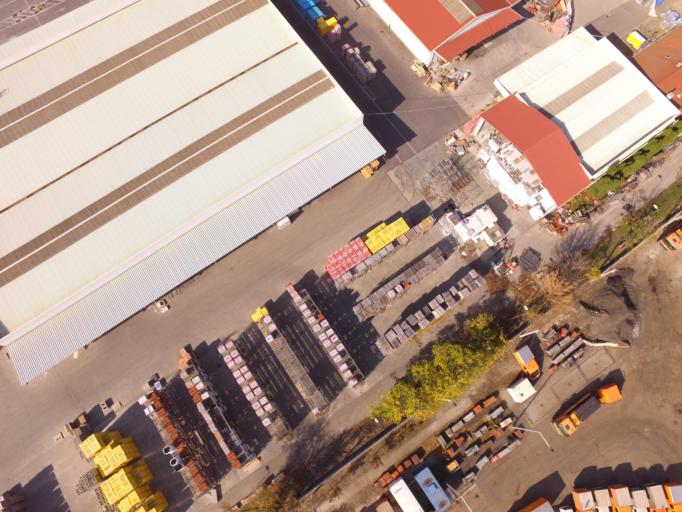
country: HU
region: Budapest
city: Budapest XX. keruelet
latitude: 47.4733
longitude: 19.1131
